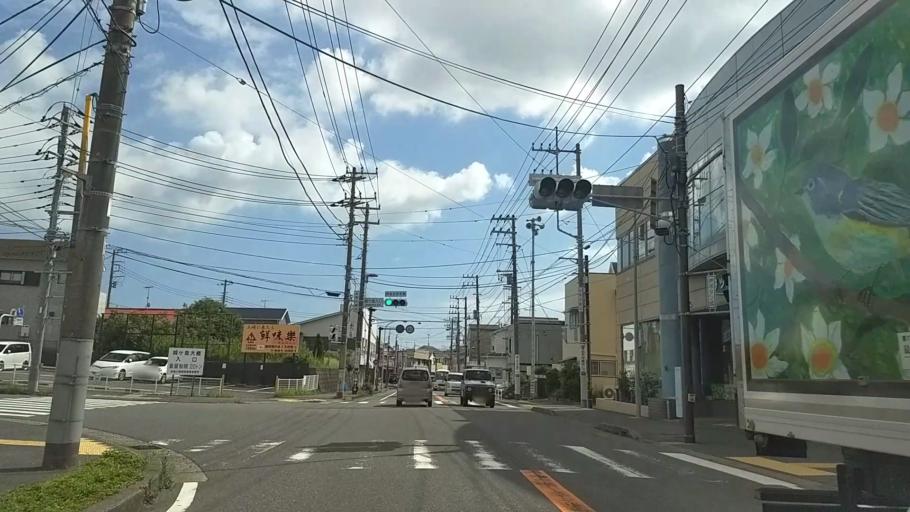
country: JP
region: Kanagawa
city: Miura
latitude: 35.1504
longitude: 139.6284
